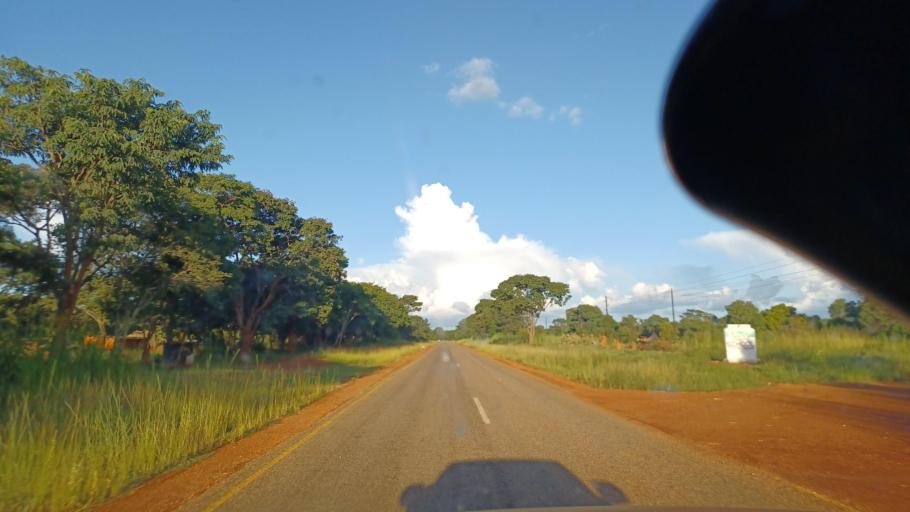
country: ZM
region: North-Western
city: Kalengwa
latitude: -13.1442
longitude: 25.0508
